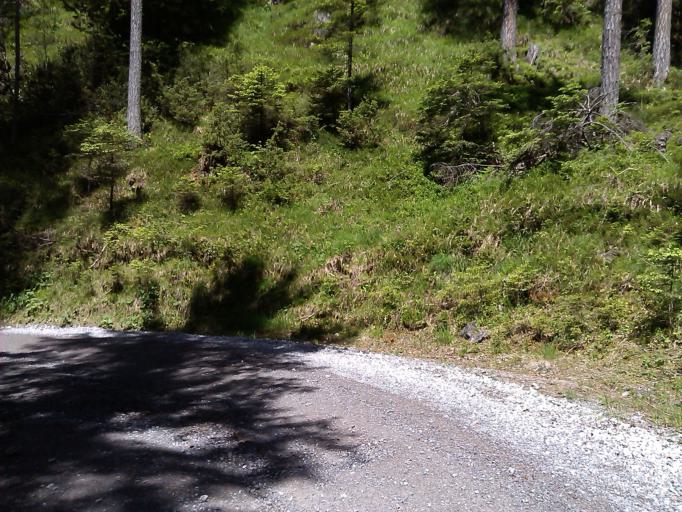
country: AT
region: Tyrol
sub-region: Politischer Bezirk Imst
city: Nassereith
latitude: 47.3563
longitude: 10.8408
